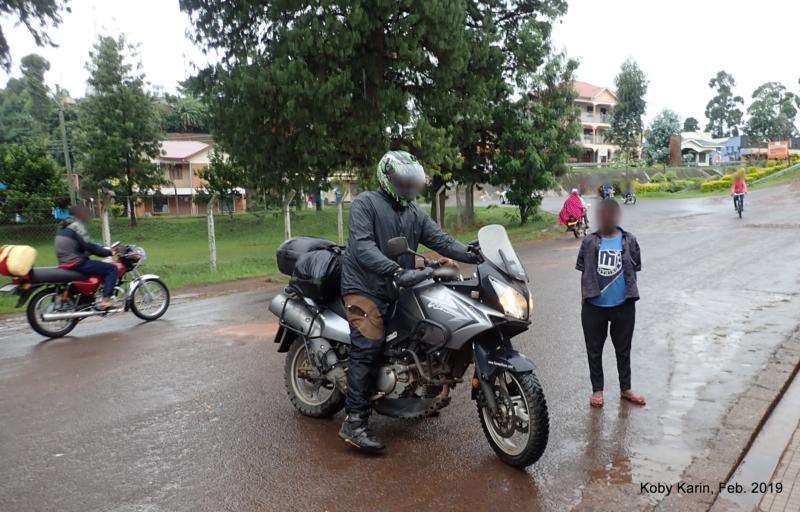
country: UG
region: Western Region
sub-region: Kisoro District
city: Kisoro
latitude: -1.2822
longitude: 29.6916
